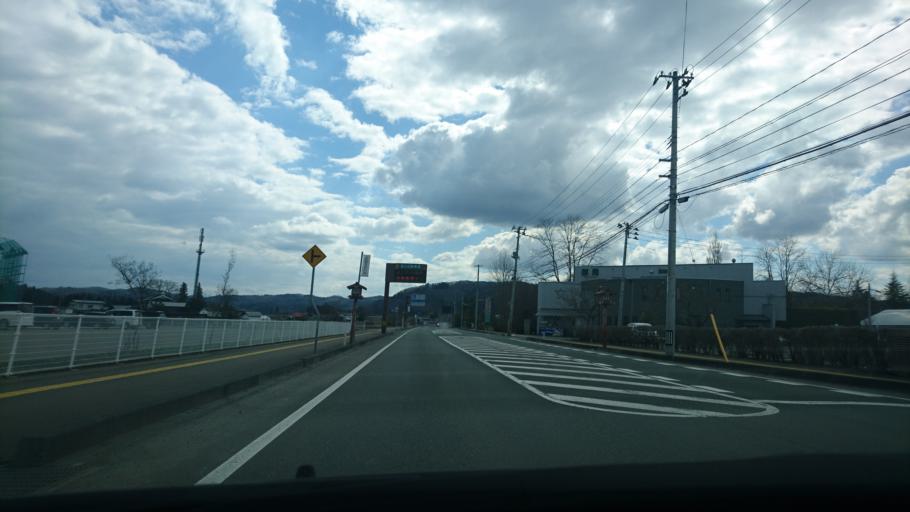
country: JP
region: Iwate
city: Hanamaki
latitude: 39.3835
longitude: 141.2247
